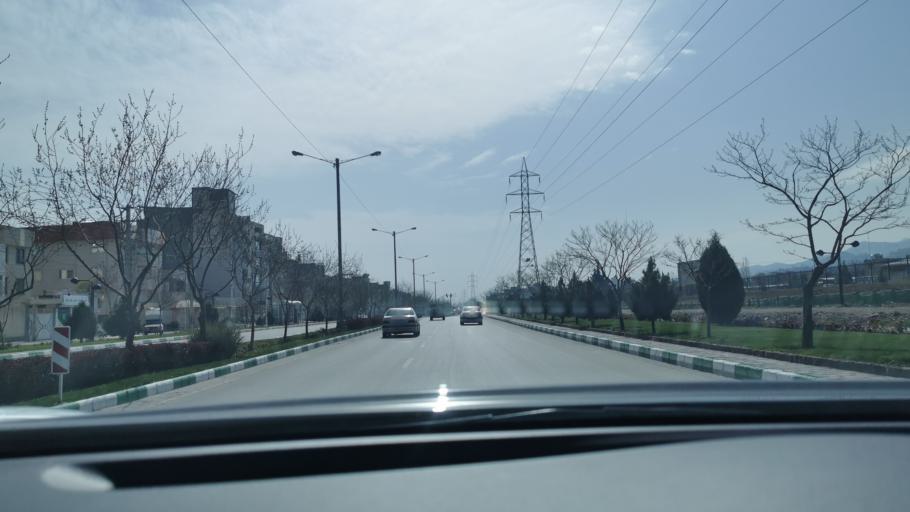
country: IR
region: Razavi Khorasan
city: Mashhad
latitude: 36.2861
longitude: 59.5385
